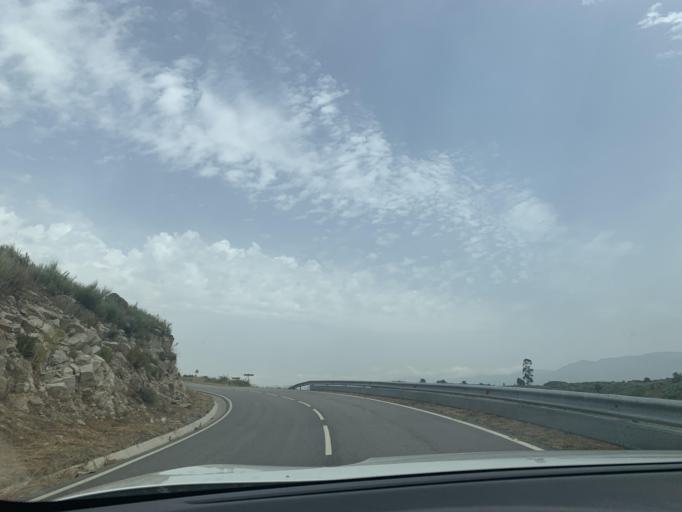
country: PT
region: Viseu
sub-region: Mangualde
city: Mangualde
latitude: 40.5710
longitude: -7.6501
